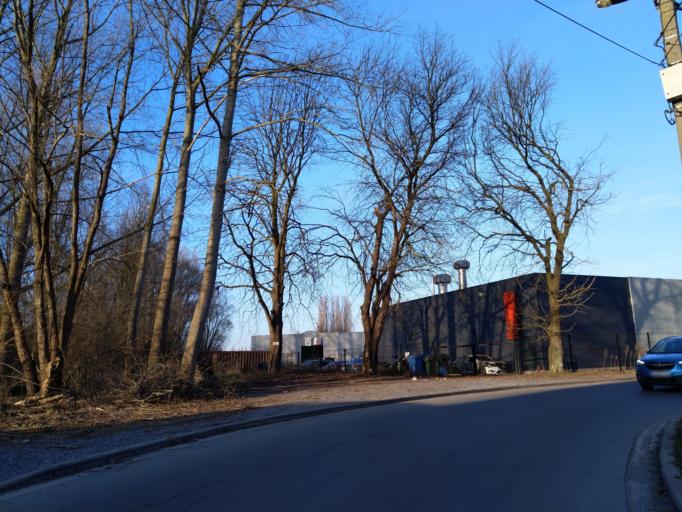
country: BE
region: Wallonia
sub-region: Province du Hainaut
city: Chasse Royale
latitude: 50.4418
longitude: 3.9201
